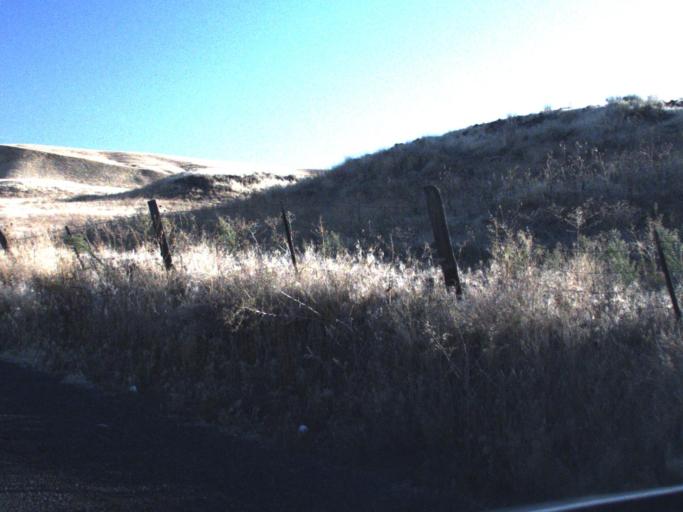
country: US
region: Washington
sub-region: Walla Walla County
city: Waitsburg
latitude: 46.6572
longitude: -118.2662
